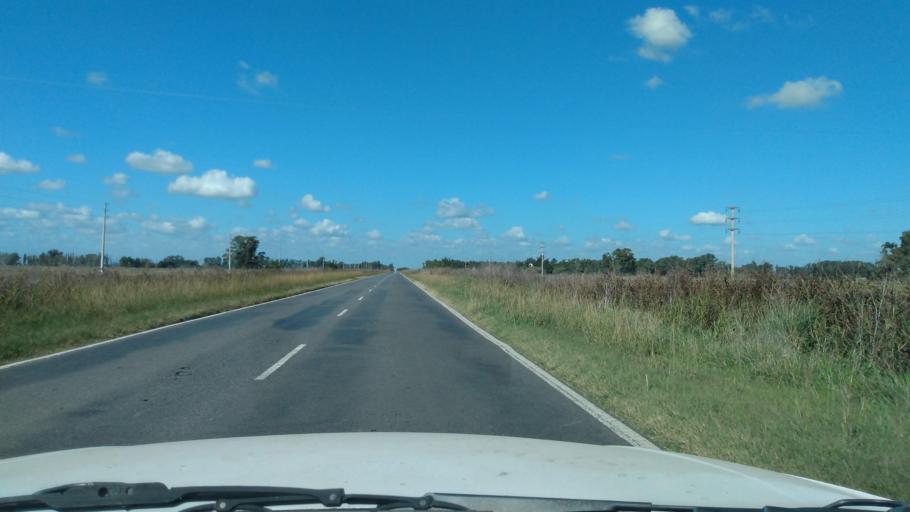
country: AR
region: Buenos Aires
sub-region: Partido de Mercedes
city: Mercedes
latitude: -34.7244
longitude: -59.3929
